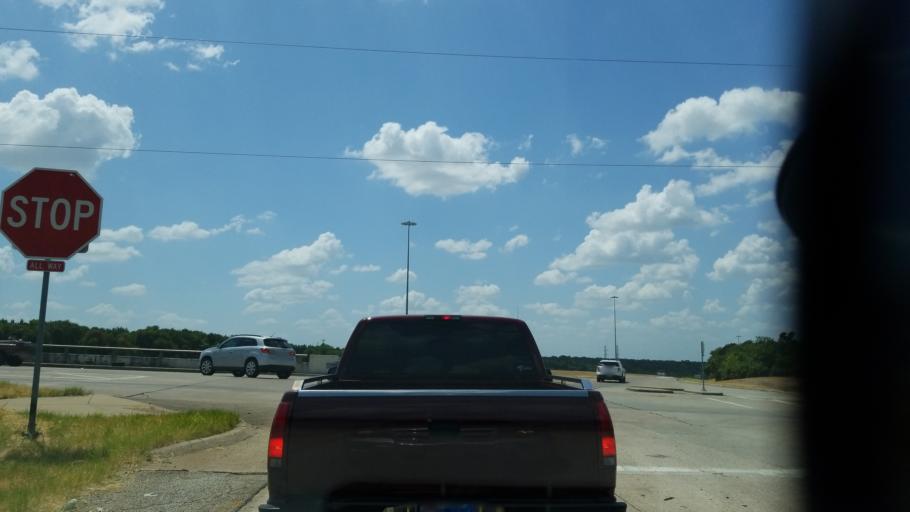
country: US
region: Texas
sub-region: Dallas County
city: Cockrell Hill
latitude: 32.7207
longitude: -96.9195
